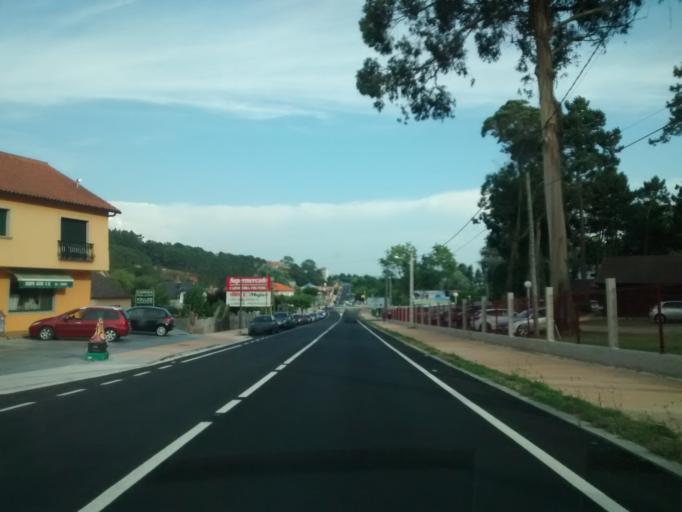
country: ES
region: Galicia
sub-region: Provincia de Pontevedra
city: Sanxenxo
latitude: 42.4185
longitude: -8.8701
